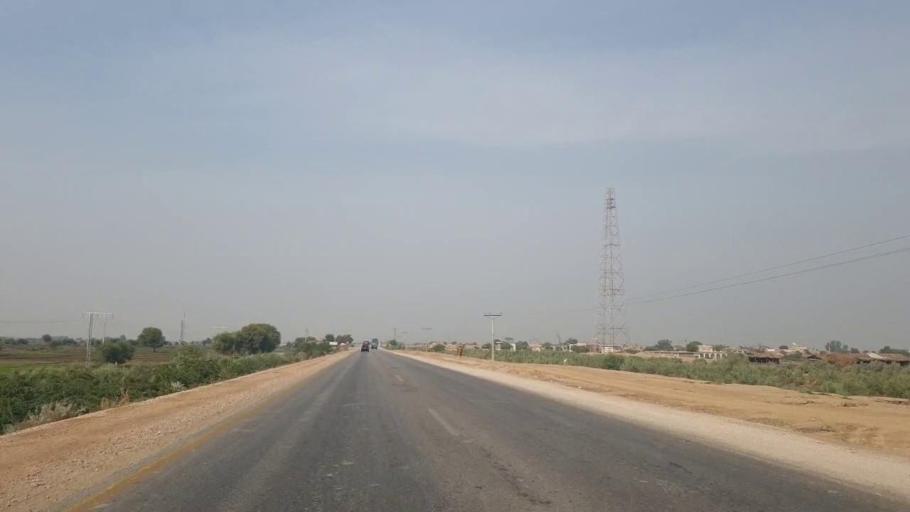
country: PK
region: Sindh
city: Sann
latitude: 26.0848
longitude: 68.0927
